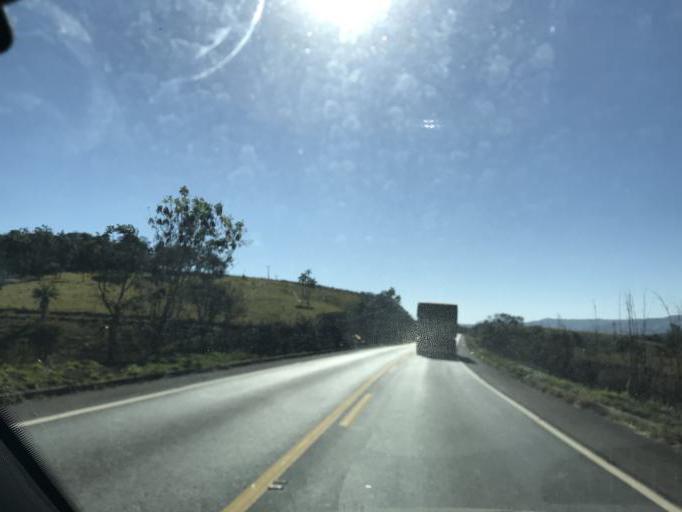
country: BR
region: Minas Gerais
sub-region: Bambui
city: Bambui
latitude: -19.8521
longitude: -45.9958
